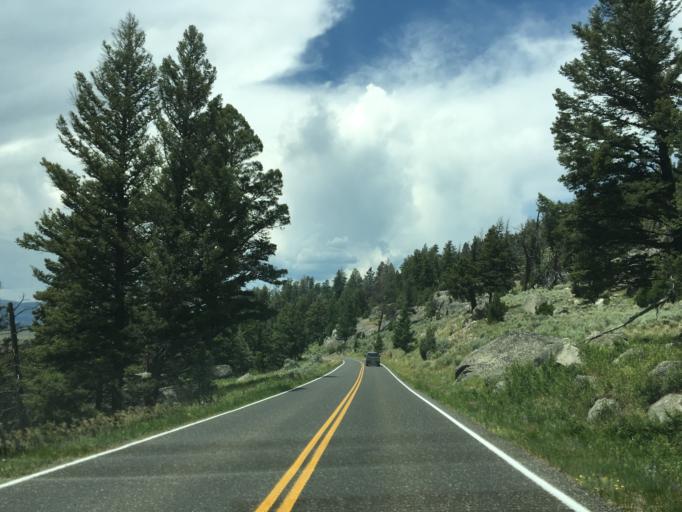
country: US
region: Montana
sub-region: Park County
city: Livingston
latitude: 44.9184
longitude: -110.2933
